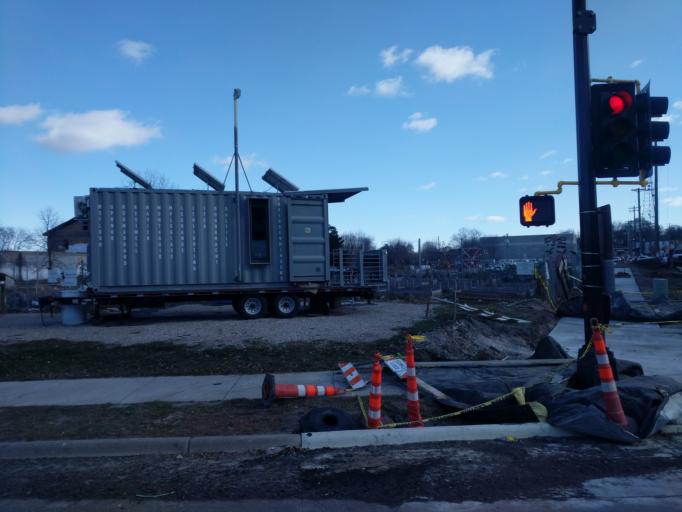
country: US
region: Minnesota
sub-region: Ramsey County
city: Lauderdale
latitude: 44.9723
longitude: -93.2152
